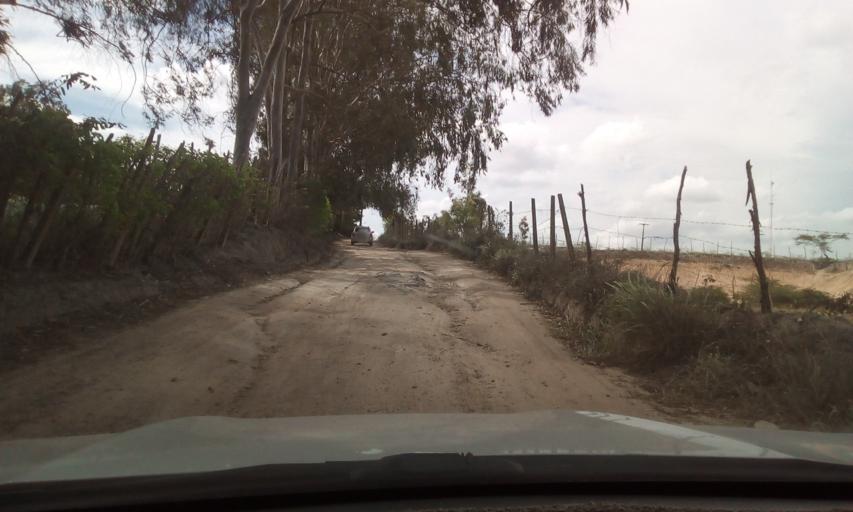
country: BR
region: Pernambuco
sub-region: Cha Grande
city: Cha Grande
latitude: -8.1881
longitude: -35.4989
